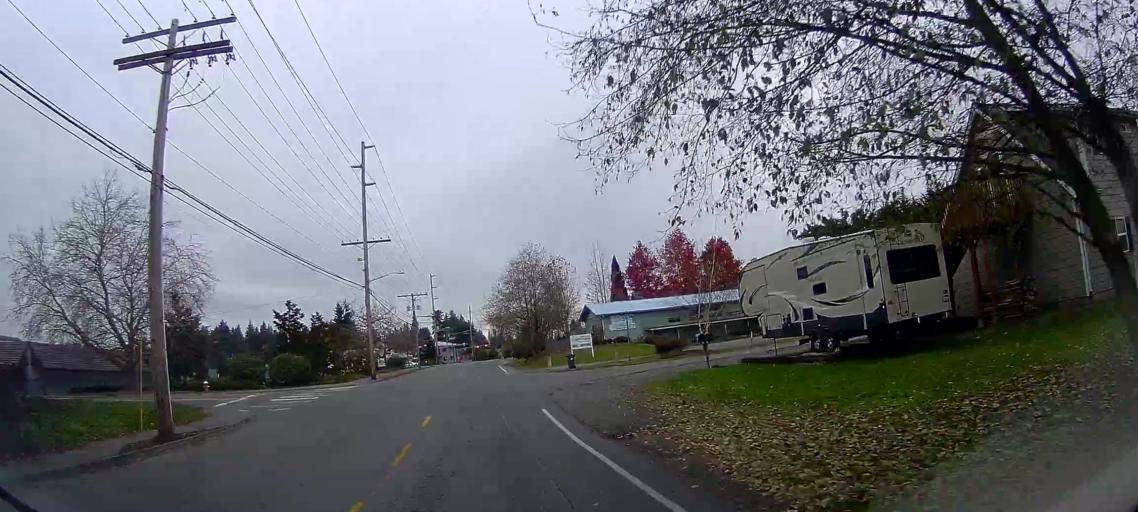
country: US
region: Washington
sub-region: Skagit County
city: Mount Vernon
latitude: 48.4337
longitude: -122.3190
